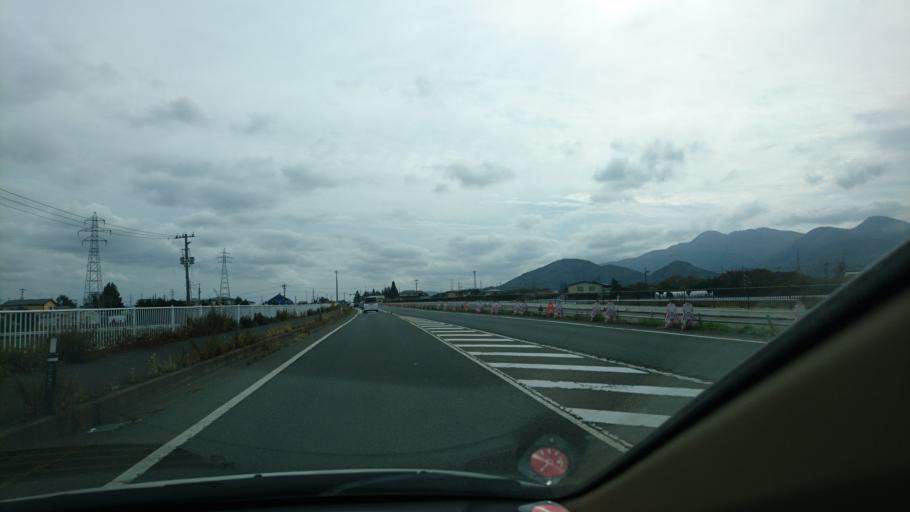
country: JP
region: Iwate
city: Morioka-shi
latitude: 39.6993
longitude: 141.1030
